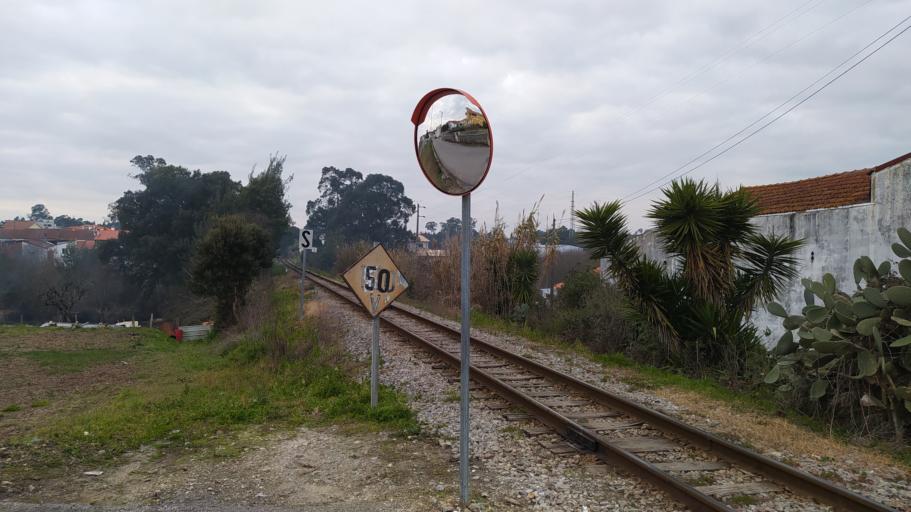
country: PT
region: Aveiro
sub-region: Aveiro
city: Eixo
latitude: 40.6317
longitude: -8.5699
